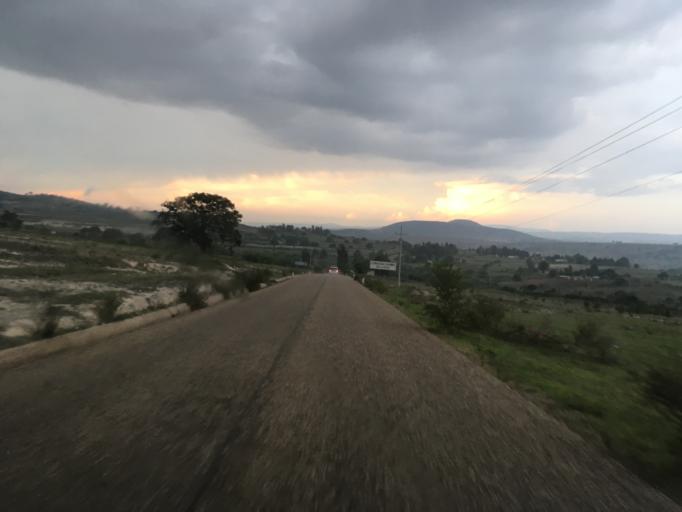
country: MX
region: Oaxaca
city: Santiago Tilantongo
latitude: 17.2824
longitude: -97.2899
